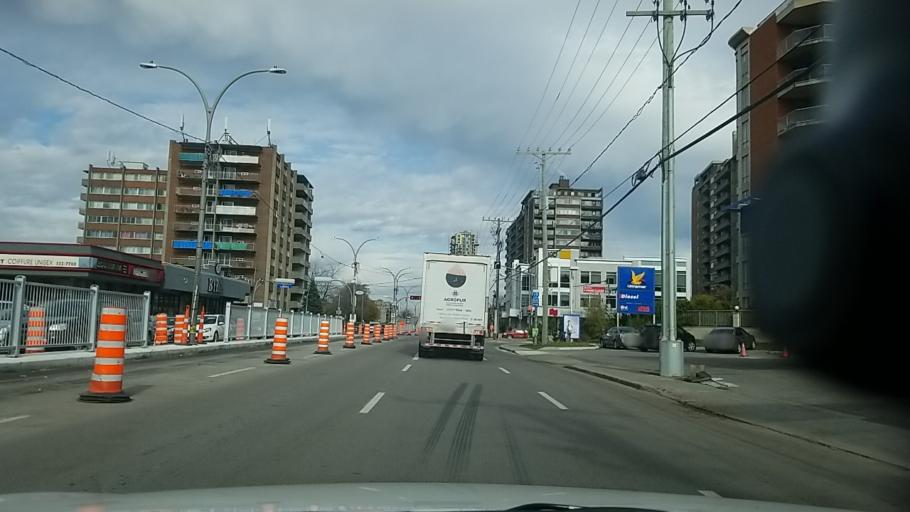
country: CA
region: Quebec
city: Mont-Royal
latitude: 45.5281
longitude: -73.6693
